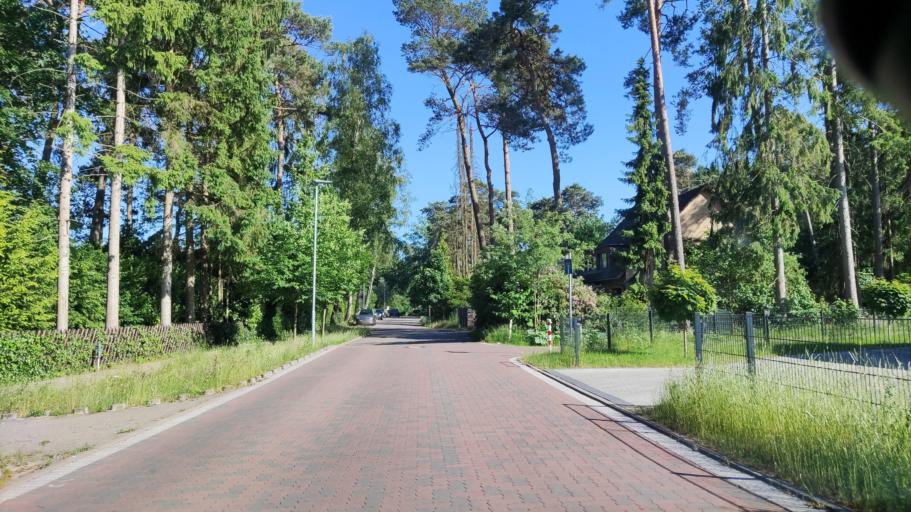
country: DE
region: Lower Saxony
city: Harmstorf
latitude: 53.3753
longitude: 10.0377
